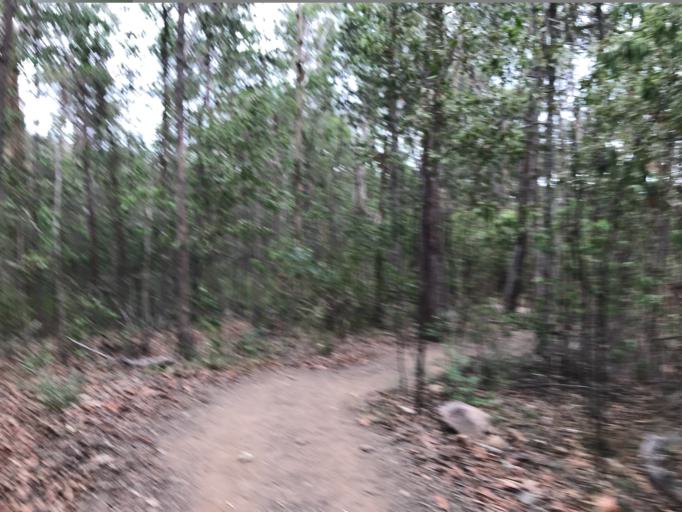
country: AU
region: Queensland
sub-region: Brisbane
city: Taringa
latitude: -27.4701
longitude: 152.9505
